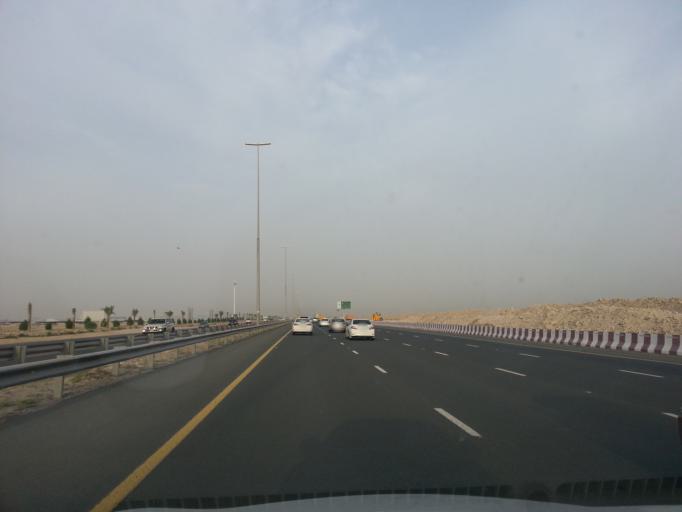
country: AE
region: Dubai
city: Dubai
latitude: 24.9345
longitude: 55.0257
